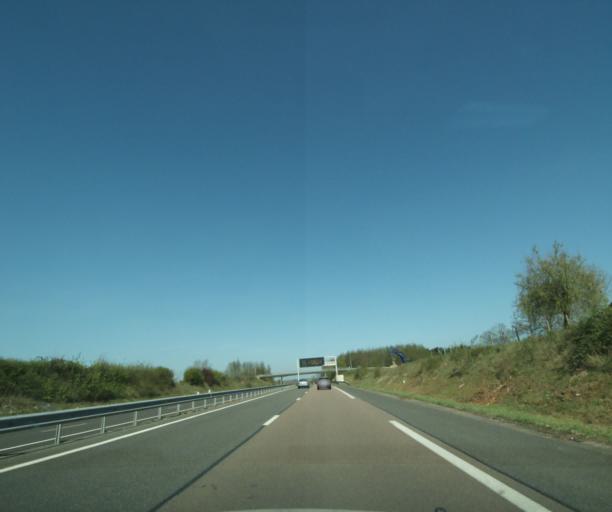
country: FR
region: Bourgogne
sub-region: Departement de la Nievre
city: Cosne-Cours-sur-Loire
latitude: 47.3950
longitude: 2.9337
